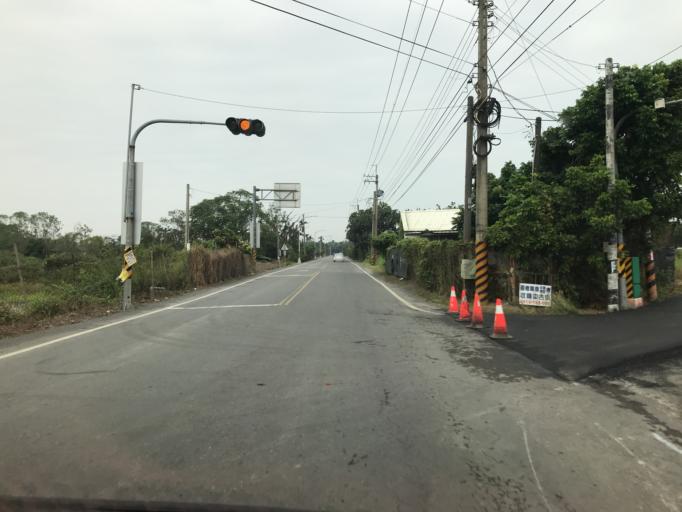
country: TW
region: Taiwan
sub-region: Pingtung
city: Pingtung
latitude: 22.4719
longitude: 120.6077
